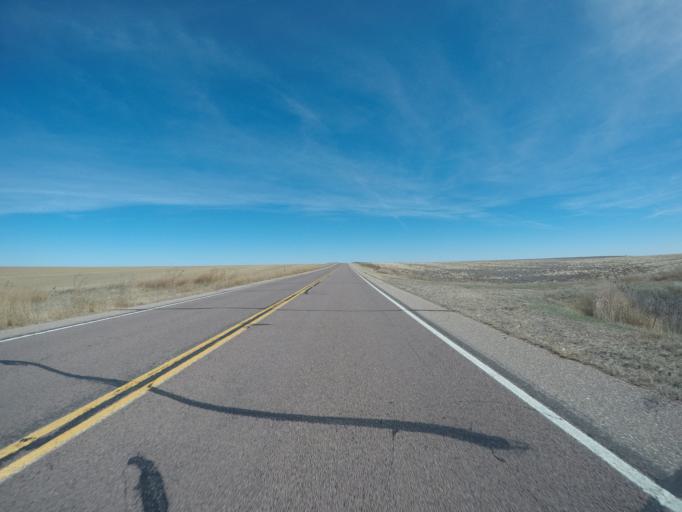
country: US
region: Colorado
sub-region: Kit Carson County
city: Burlington
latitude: 39.6579
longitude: -102.4994
